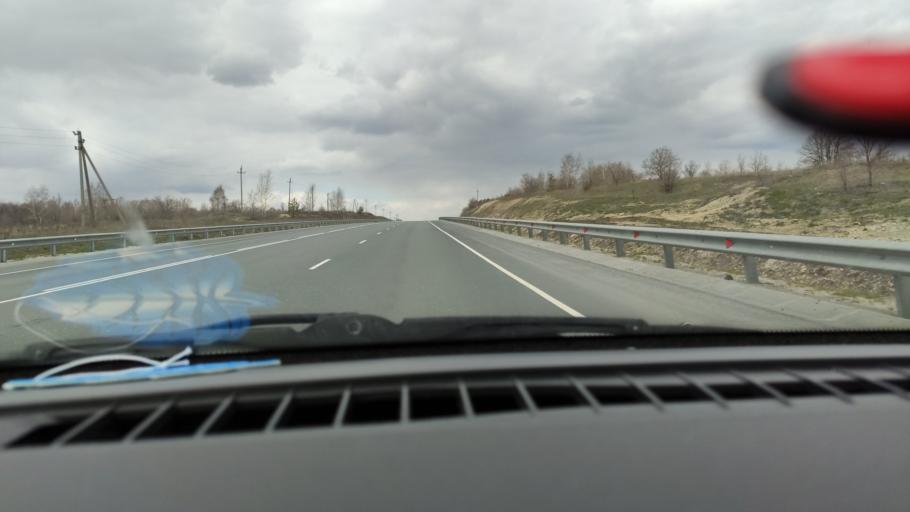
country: RU
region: Saratov
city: Shikhany
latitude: 52.1452
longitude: 47.1991
